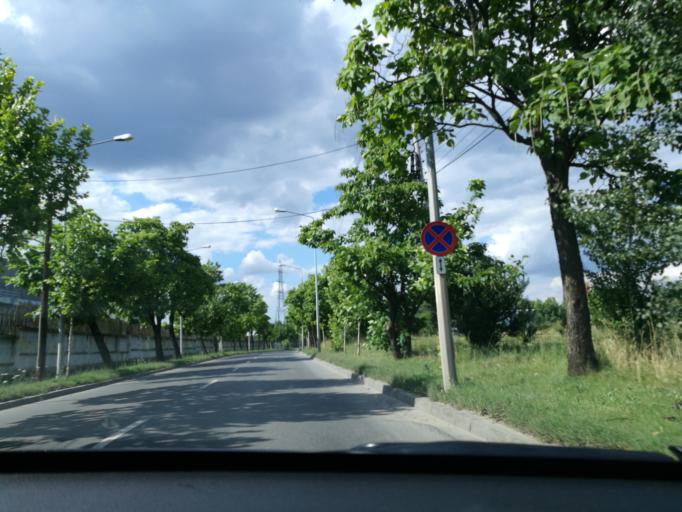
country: RO
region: Ilfov
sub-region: Comuna Glina
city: Catelu
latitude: 44.4159
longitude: 26.2178
